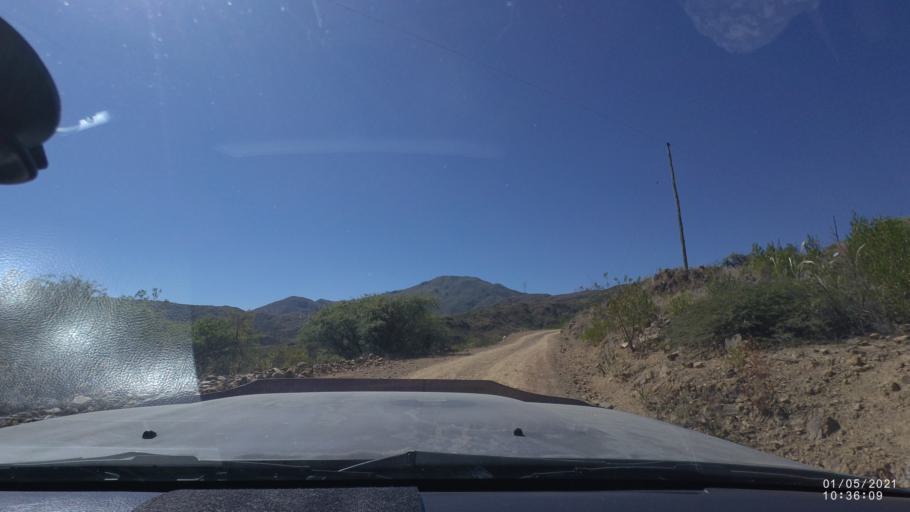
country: BO
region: Cochabamba
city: Capinota
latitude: -17.5993
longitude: -66.1885
